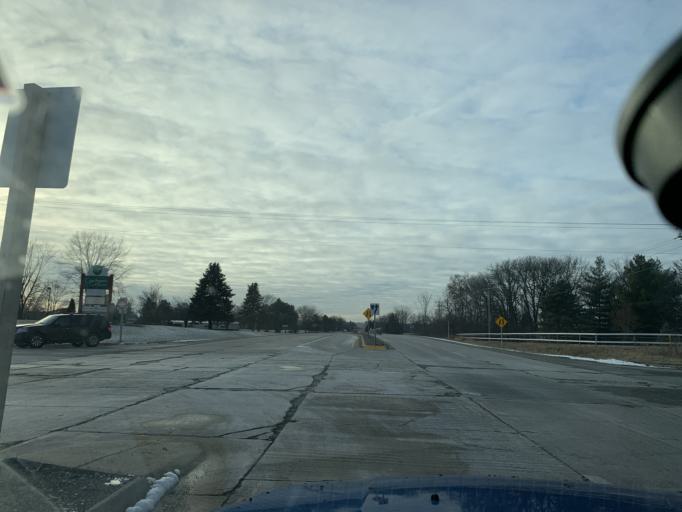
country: US
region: Wisconsin
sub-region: Rock County
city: Edgerton
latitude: 42.9211
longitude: -89.0915
